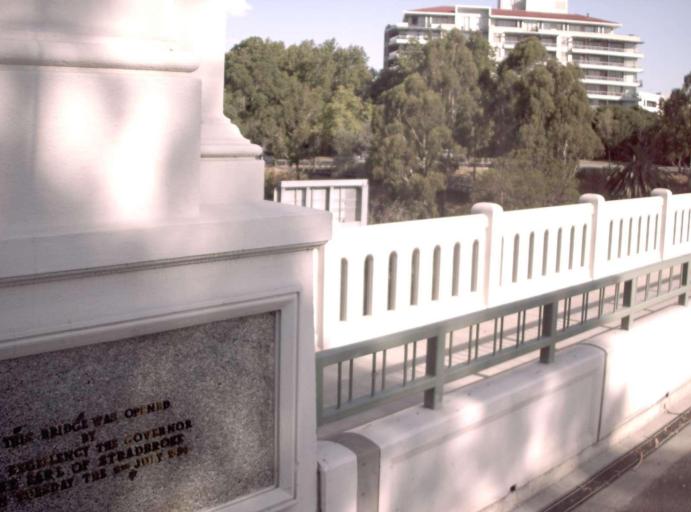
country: AU
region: Victoria
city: Albert Park
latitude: -37.8337
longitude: 144.9967
